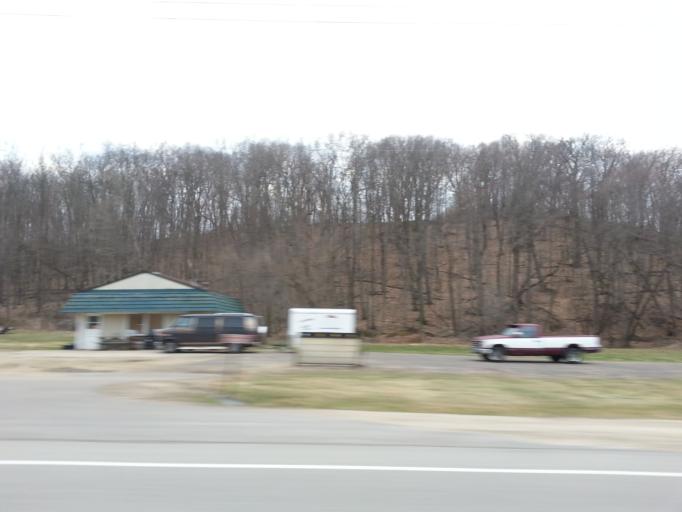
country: US
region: Wisconsin
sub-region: Pierce County
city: Ellsworth
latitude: 44.7321
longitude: -92.5068
